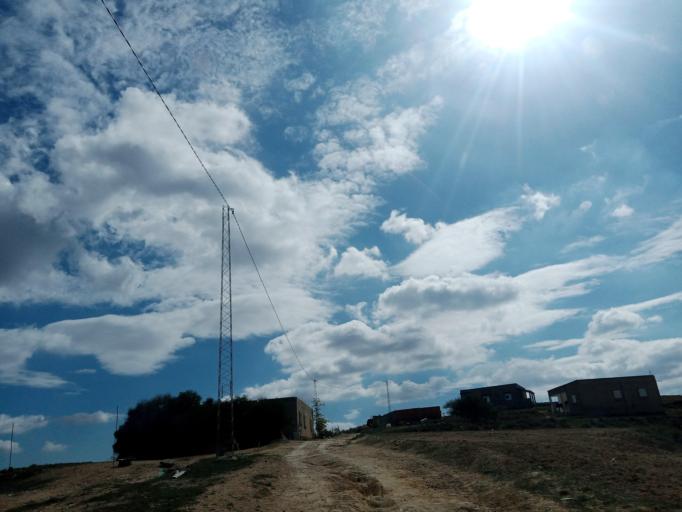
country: TN
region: Tunis
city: Oued Lill
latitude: 36.8101
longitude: 9.9822
